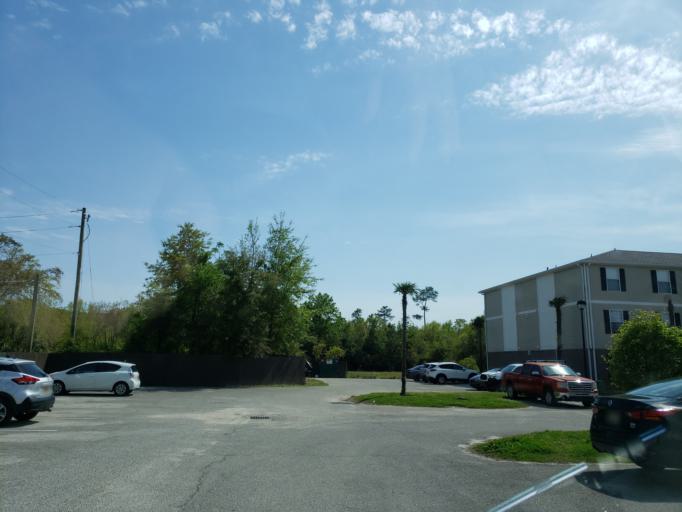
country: US
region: Mississippi
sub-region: Harrison County
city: D'Iberville
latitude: 30.3942
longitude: -88.9825
